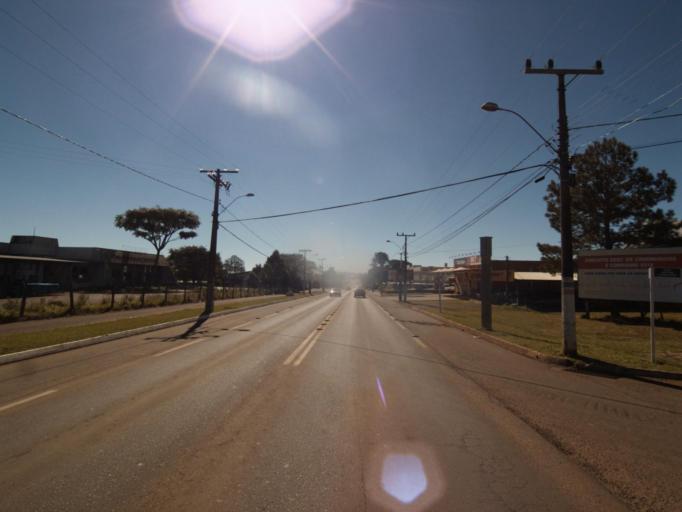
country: AR
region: Misiones
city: Bernardo de Irigoyen
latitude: -26.7462
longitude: -53.5185
